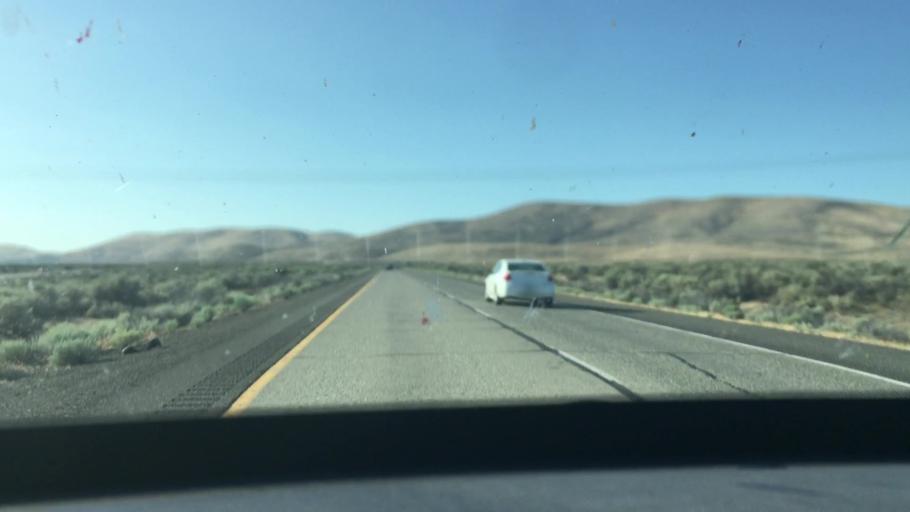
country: US
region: Washington
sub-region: Kittitas County
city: Kittitas
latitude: 46.8287
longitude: -120.3673
